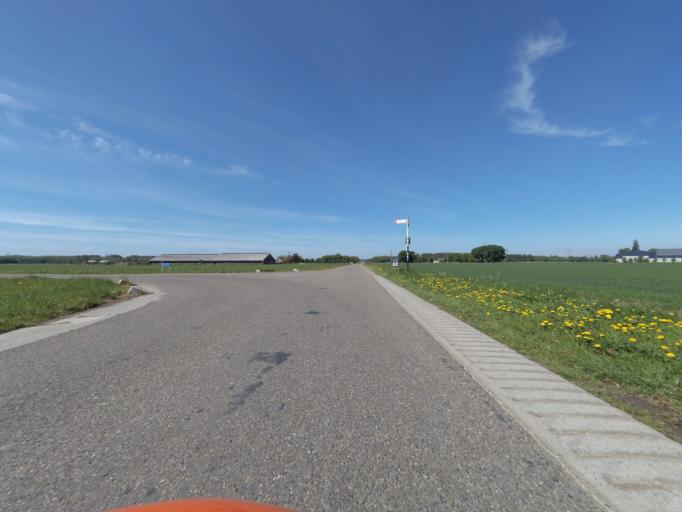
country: NL
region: Flevoland
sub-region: Gemeente Dronten
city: Biddinghuizen
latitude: 52.4152
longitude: 5.6396
